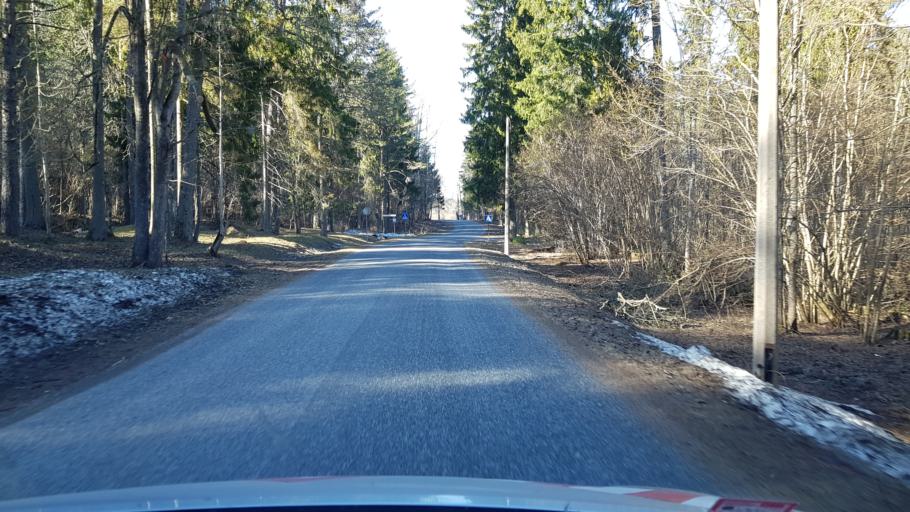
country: EE
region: Laeaene-Virumaa
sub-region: Vinni vald
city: Vinni
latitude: 59.1686
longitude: 26.5911
